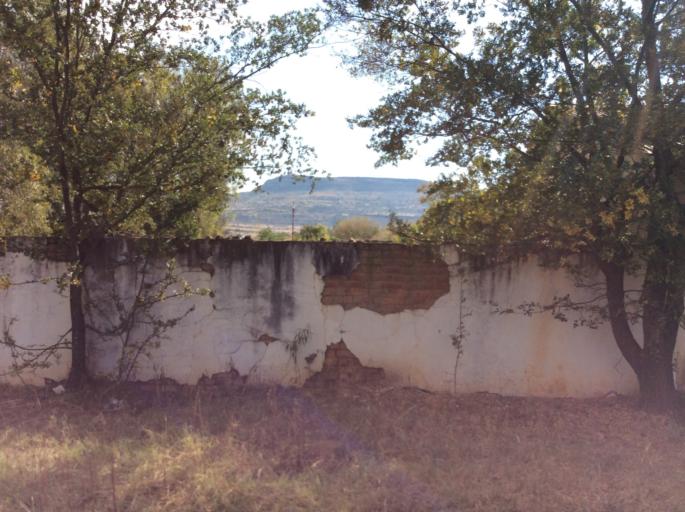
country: LS
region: Mafeteng
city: Mafeteng
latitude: -29.7290
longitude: 27.0271
